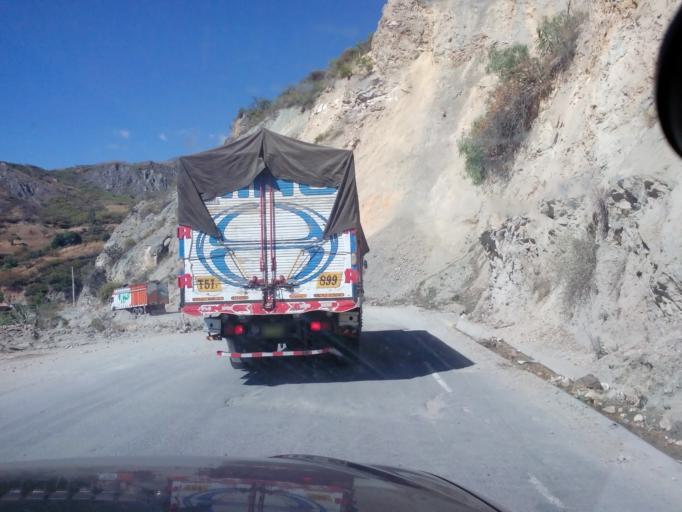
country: PE
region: Apurimac
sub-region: Provincia de Abancay
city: Curahuasi
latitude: -13.5458
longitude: -72.6757
